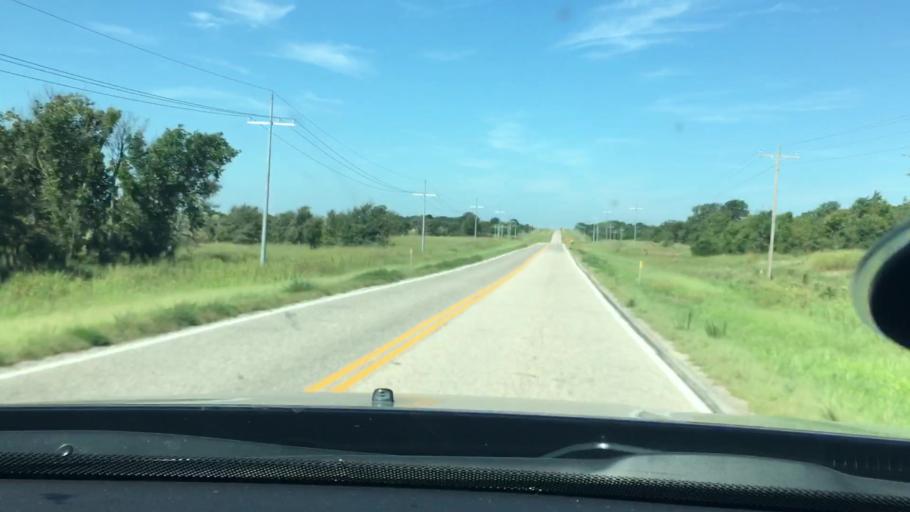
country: US
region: Oklahoma
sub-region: Johnston County
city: Tishomingo
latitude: 34.3612
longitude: -96.6171
